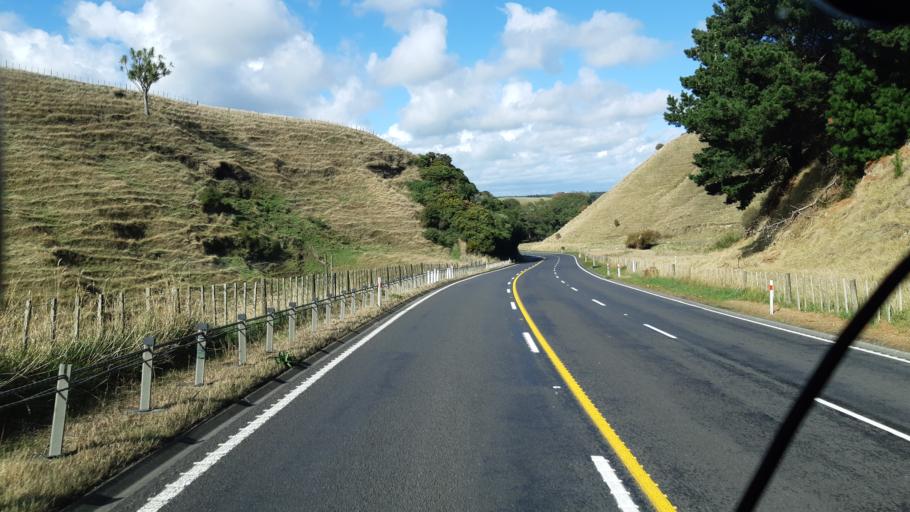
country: NZ
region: Manawatu-Wanganui
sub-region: Wanganui District
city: Wanganui
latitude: -40.0300
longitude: 175.2030
